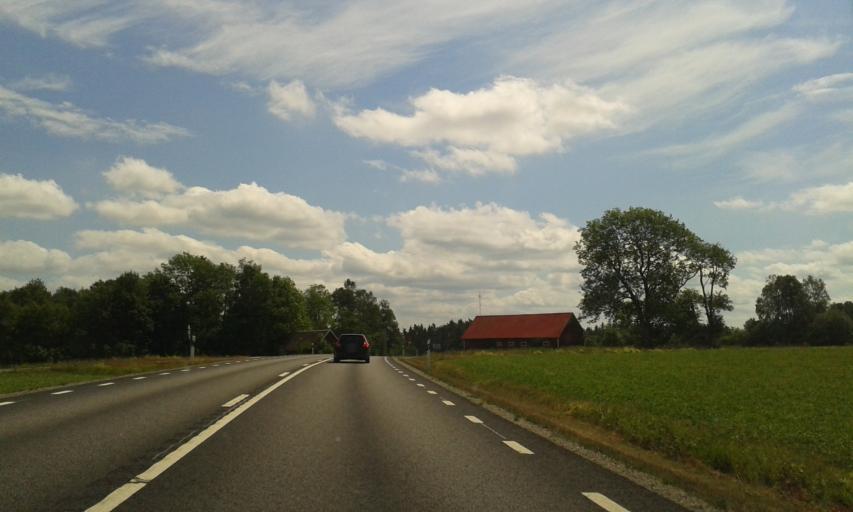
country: SE
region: Joenkoeping
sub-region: Varnamo Kommun
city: Rydaholm
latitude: 56.9967
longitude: 14.2872
